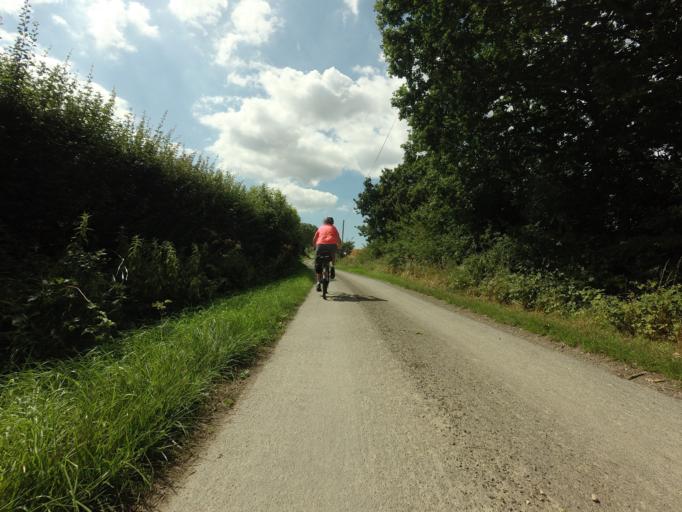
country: GB
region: England
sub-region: Kent
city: Stone
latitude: 51.0652
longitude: 0.7586
